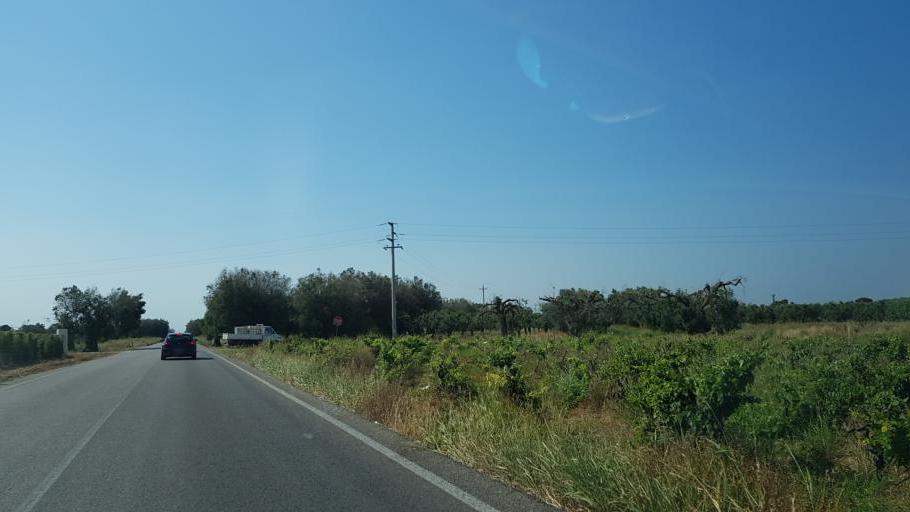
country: IT
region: Apulia
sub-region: Provincia di Lecce
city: Guagnano
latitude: 40.4063
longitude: 17.9657
